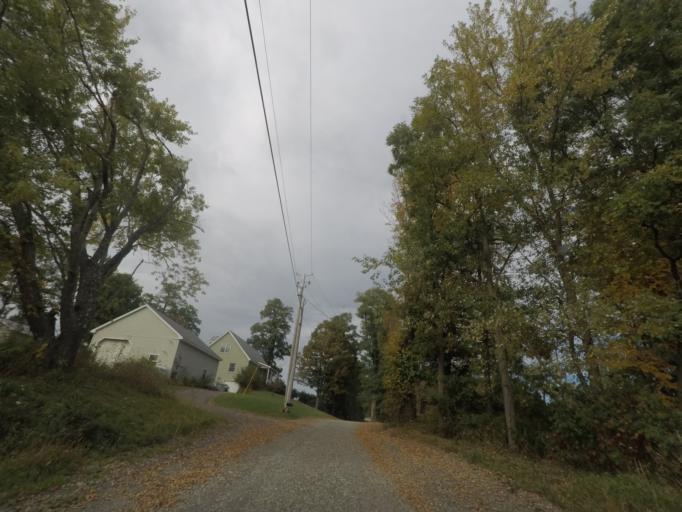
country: US
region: New York
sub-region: Rensselaer County
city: West Sand Lake
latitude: 42.5822
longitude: -73.6129
